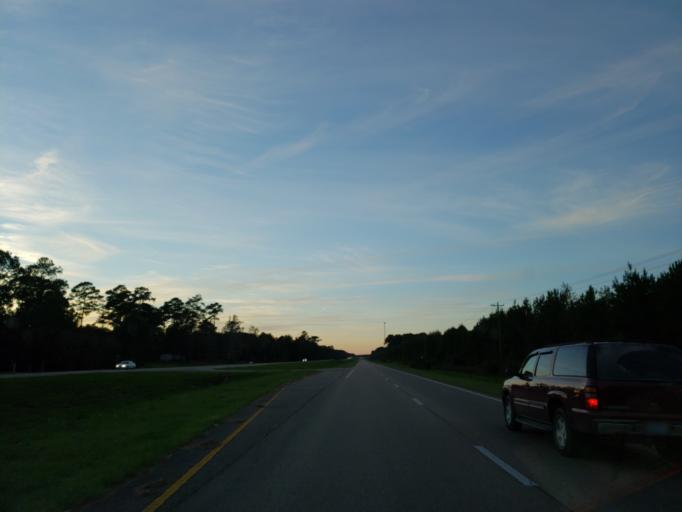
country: US
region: Mississippi
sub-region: Wayne County
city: Belmont
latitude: 31.6063
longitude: -88.5633
